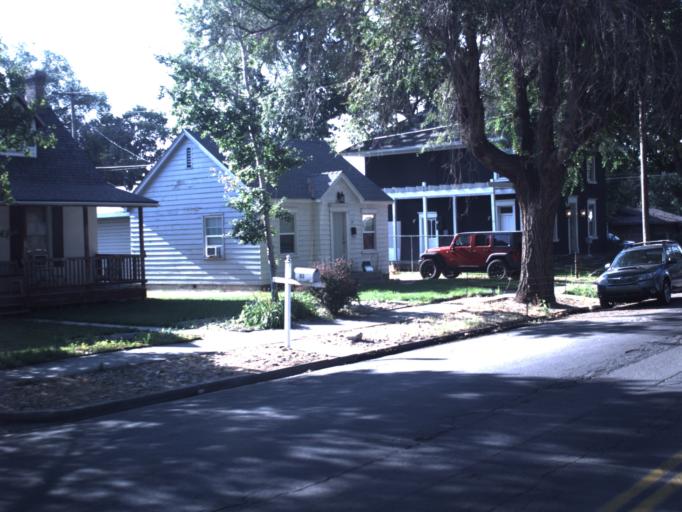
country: US
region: Utah
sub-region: Utah County
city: American Fork
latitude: 40.3753
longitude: -111.7960
